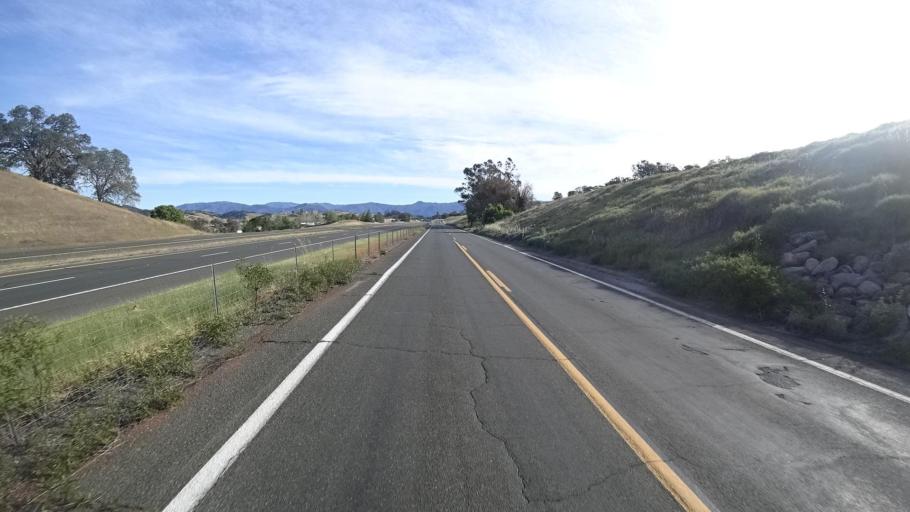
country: US
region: California
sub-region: Lake County
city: North Lakeport
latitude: 39.0949
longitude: -122.9143
